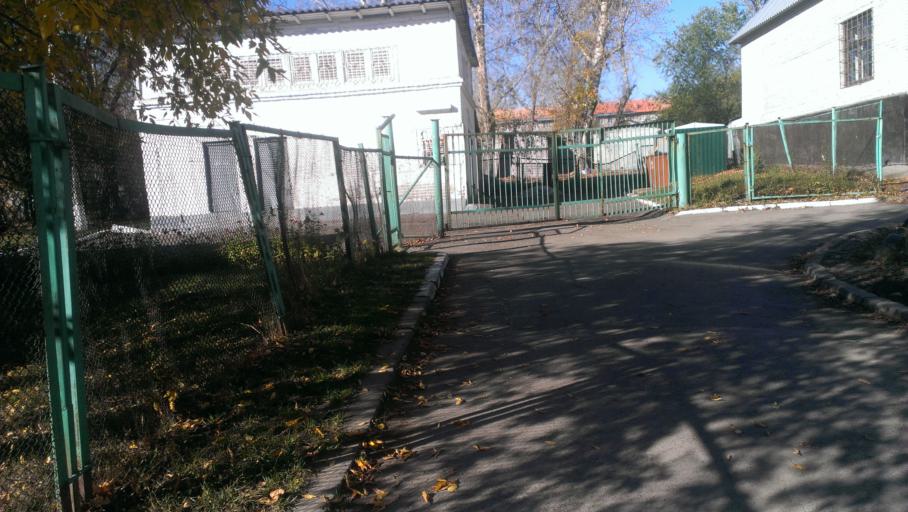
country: RU
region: Altai Krai
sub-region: Gorod Barnaulskiy
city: Barnaul
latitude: 53.3643
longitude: 83.6847
